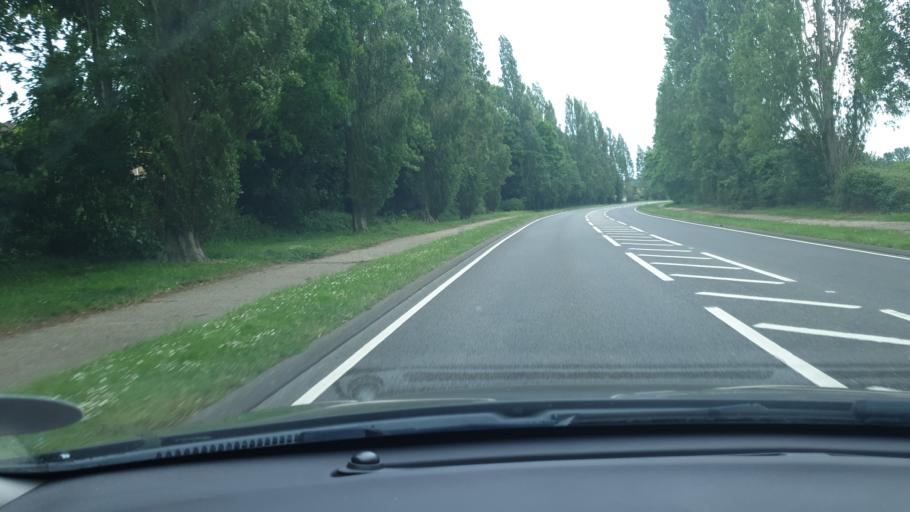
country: GB
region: England
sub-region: Essex
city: Little Clacton
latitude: 51.8578
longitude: 1.1121
